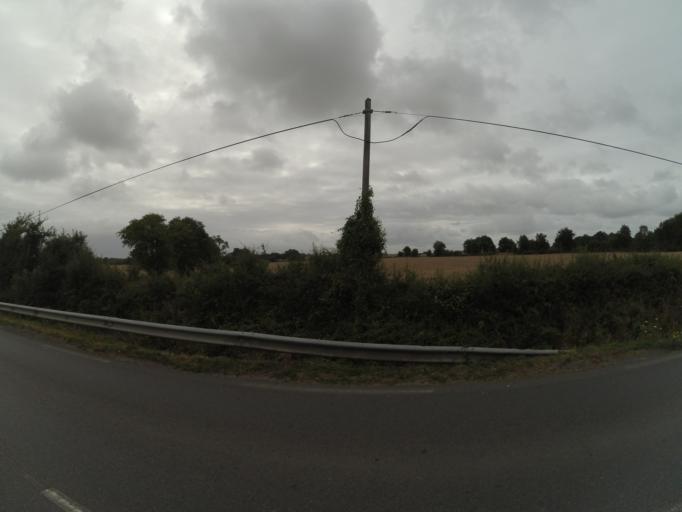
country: FR
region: Pays de la Loire
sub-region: Departement de la Loire-Atlantique
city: Lege
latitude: 46.9044
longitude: -1.5646
